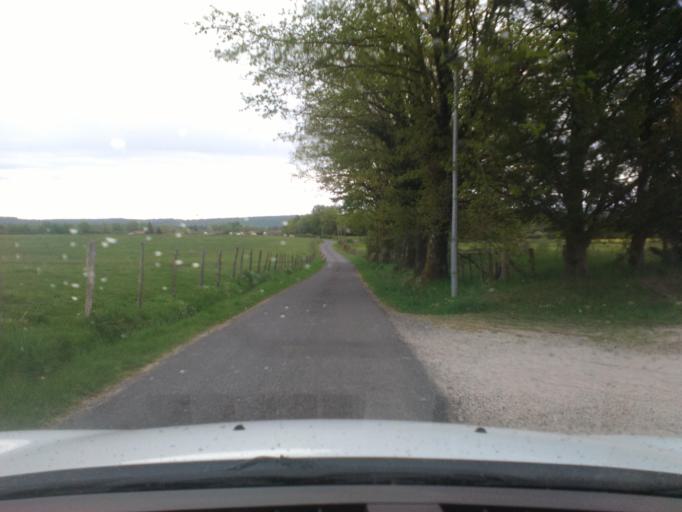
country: FR
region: Rhone-Alpes
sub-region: Departement de l'Ain
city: Saint-Etienne-du-Bois
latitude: 46.2430
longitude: 5.2875
